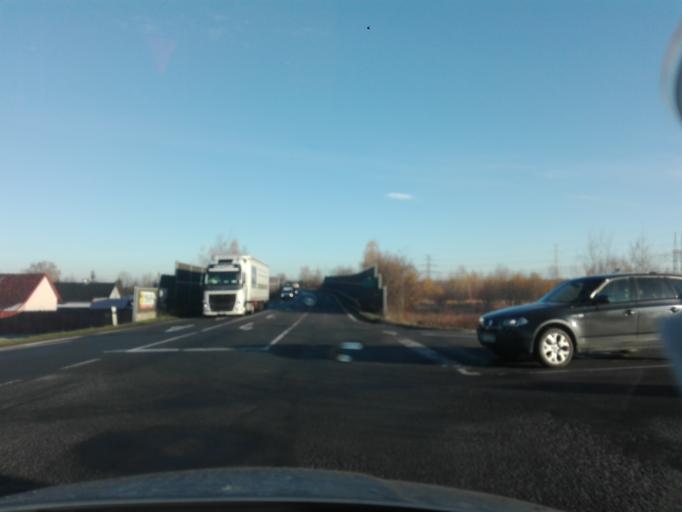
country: CZ
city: Dobra
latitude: 49.6717
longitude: 18.4249
